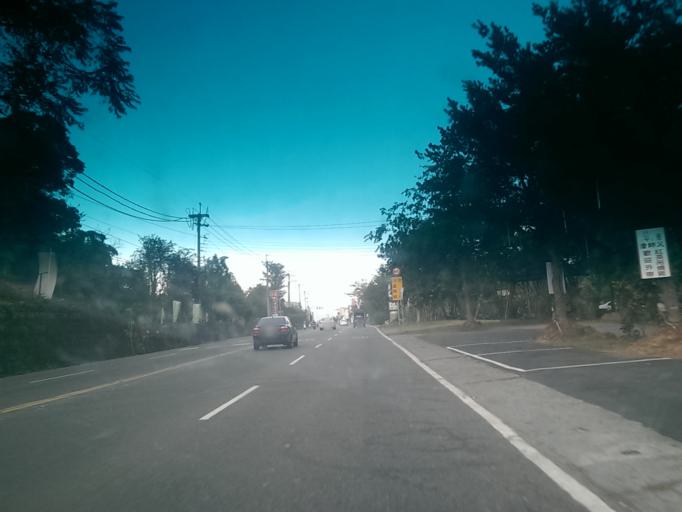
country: TW
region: Taiwan
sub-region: Nantou
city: Puli
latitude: 23.9587
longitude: 120.9445
